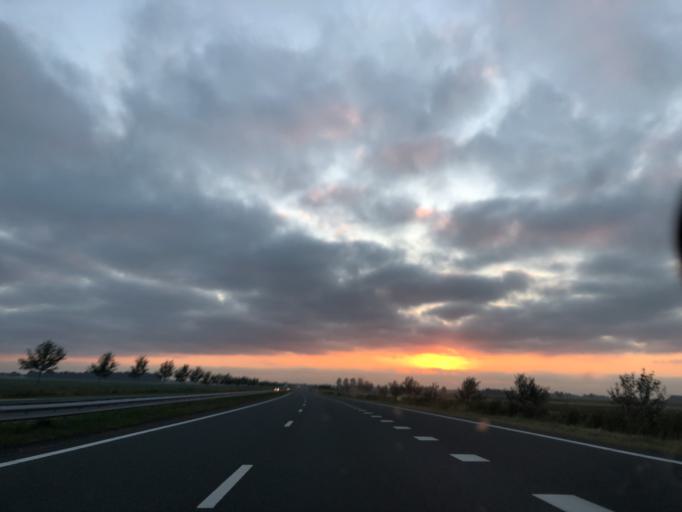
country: NL
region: Groningen
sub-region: Gemeente Veendam
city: Veendam
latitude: 53.0535
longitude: 6.8589
